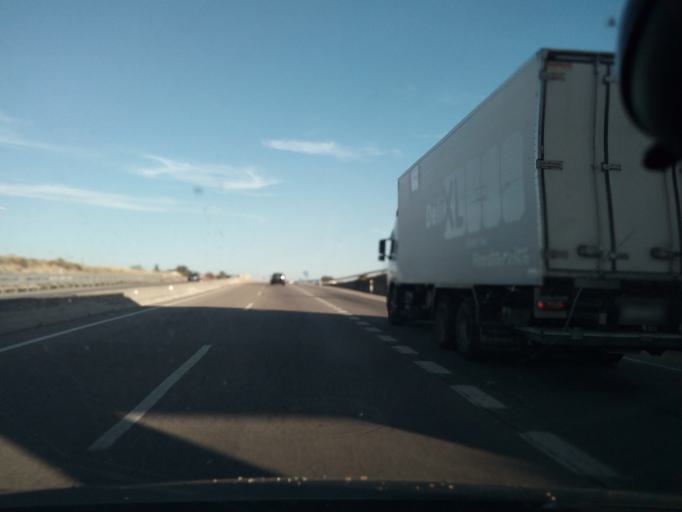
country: ES
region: Castille-La Mancha
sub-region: Province of Toledo
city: Tembleque
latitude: 39.7825
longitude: -3.4821
